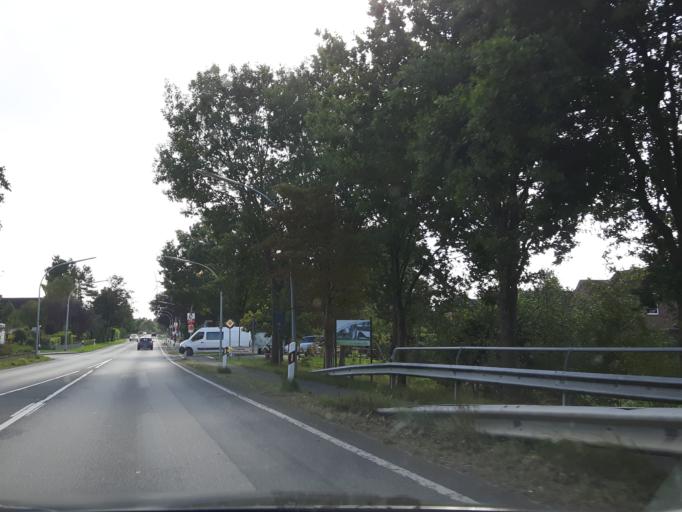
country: DE
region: Lower Saxony
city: Hatten
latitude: 53.0606
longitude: 8.3528
